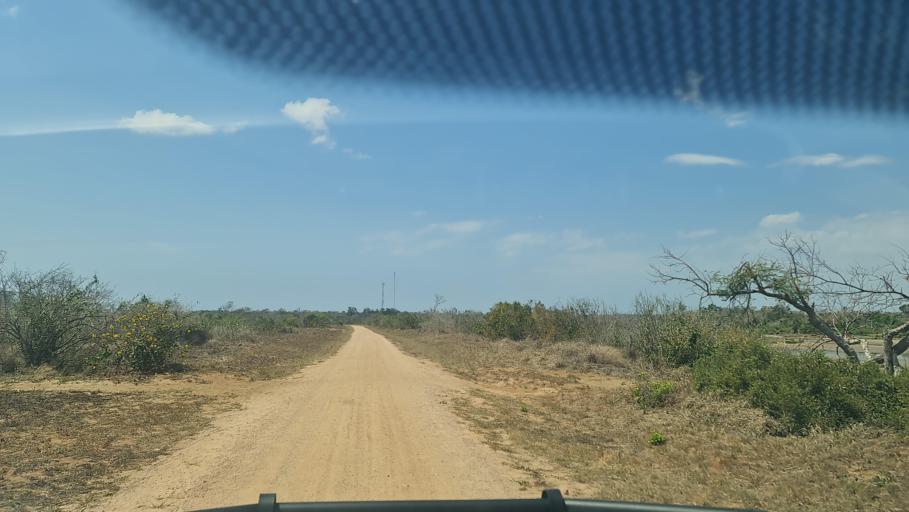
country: MZ
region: Nampula
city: Ilha de Mocambique
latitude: -15.1890
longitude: 40.5201
